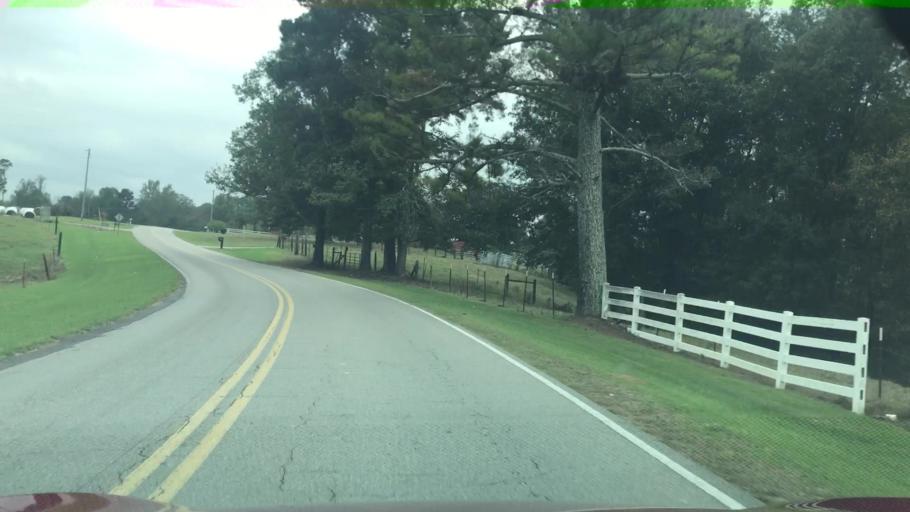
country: US
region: Alabama
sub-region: Cullman County
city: Good Hope
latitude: 34.1098
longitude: -87.0359
